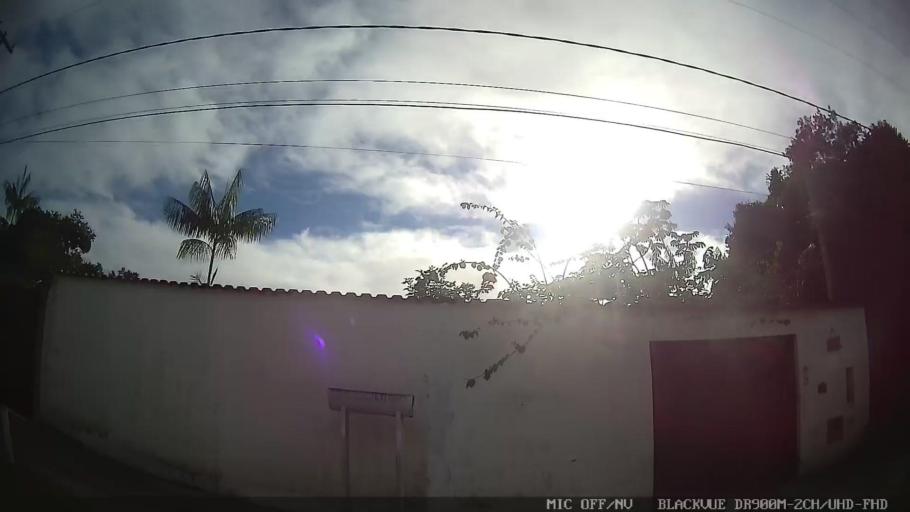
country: BR
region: Sao Paulo
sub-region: Peruibe
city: Peruibe
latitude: -24.2324
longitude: -46.9139
